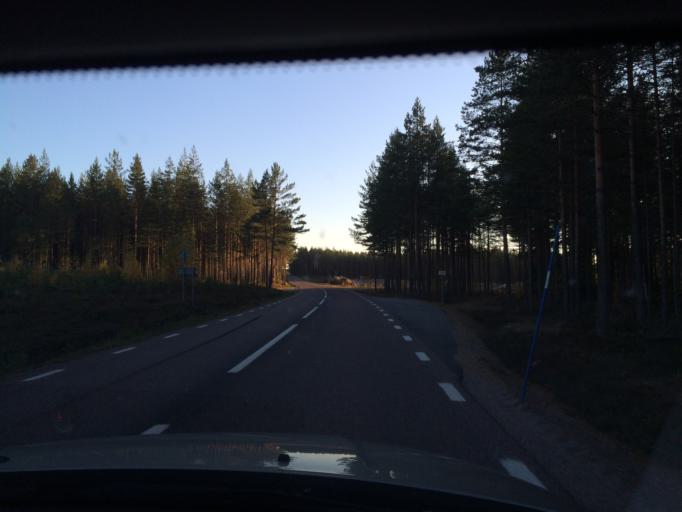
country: SE
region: Gaevleborg
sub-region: Sandvikens Kommun
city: Arsunda
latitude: 60.4764
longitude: 16.7125
